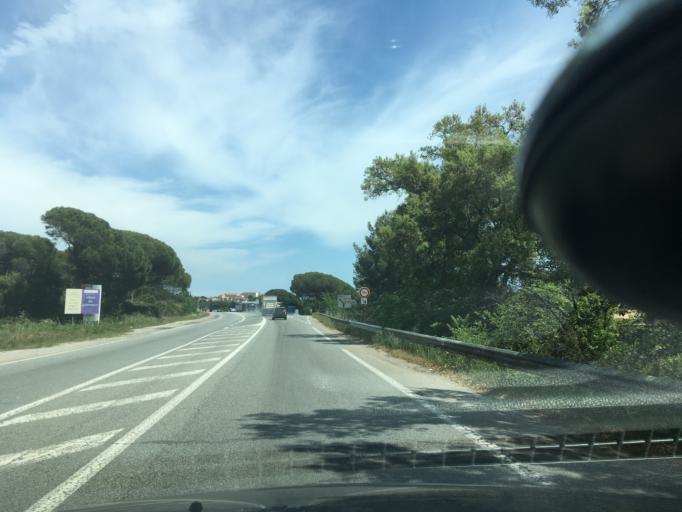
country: FR
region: Provence-Alpes-Cote d'Azur
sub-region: Departement du Var
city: Puget-sur-Argens
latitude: 43.4592
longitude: 6.6676
